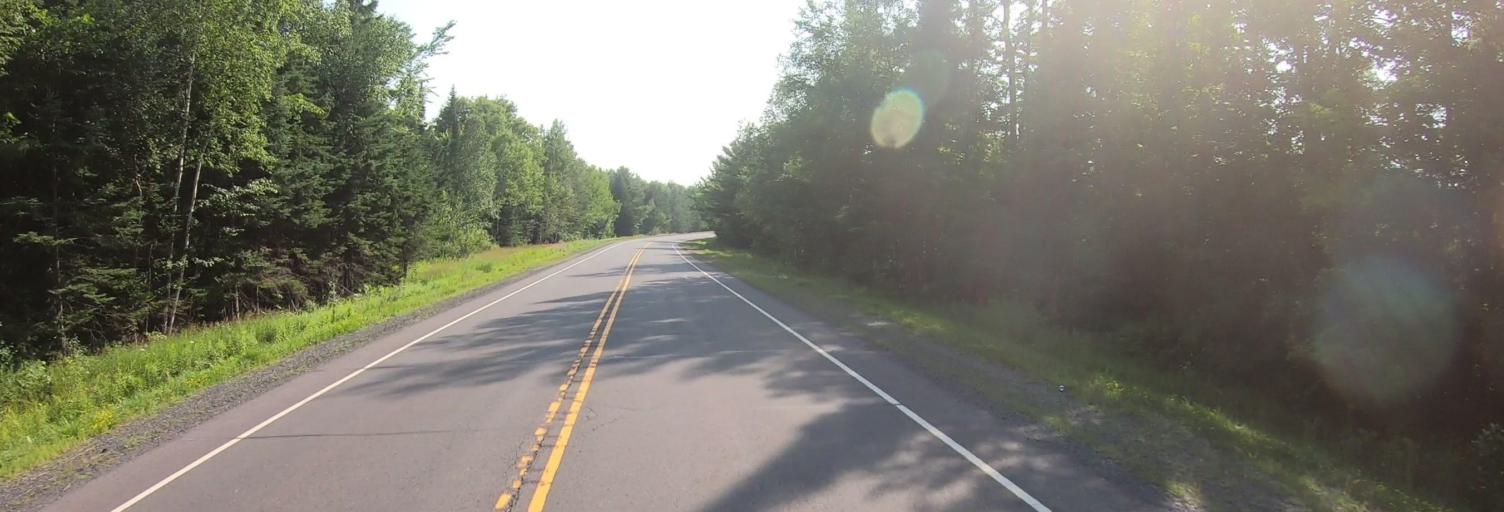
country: US
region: Wisconsin
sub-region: Iron County
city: Hurley
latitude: 46.3700
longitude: -90.3981
